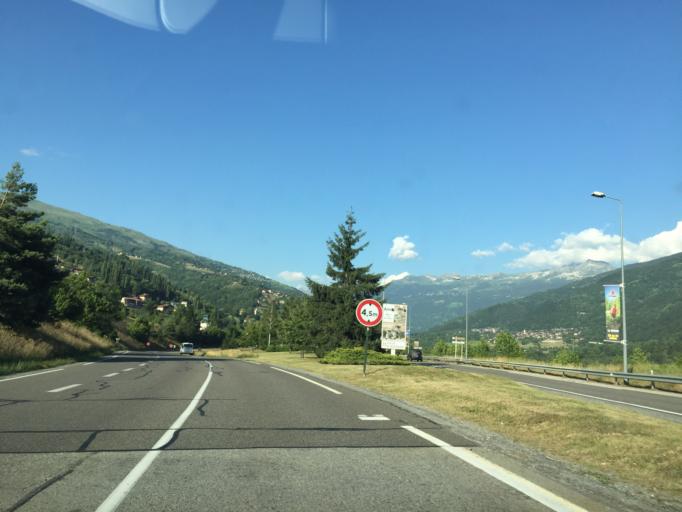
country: FR
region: Rhone-Alpes
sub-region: Departement de la Savoie
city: Aime
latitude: 45.5518
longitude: 6.6347
